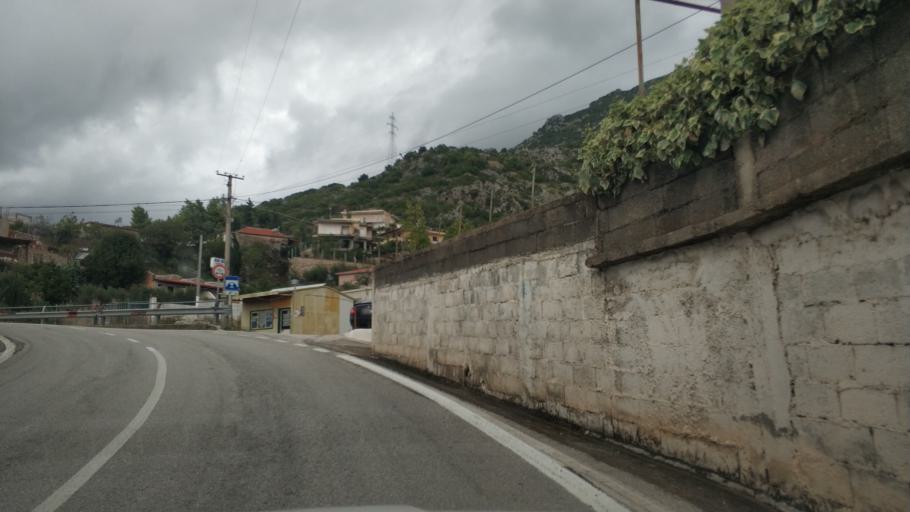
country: AL
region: Vlore
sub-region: Rrethi i Vlores
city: Vranisht
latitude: 40.1561
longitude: 19.6332
